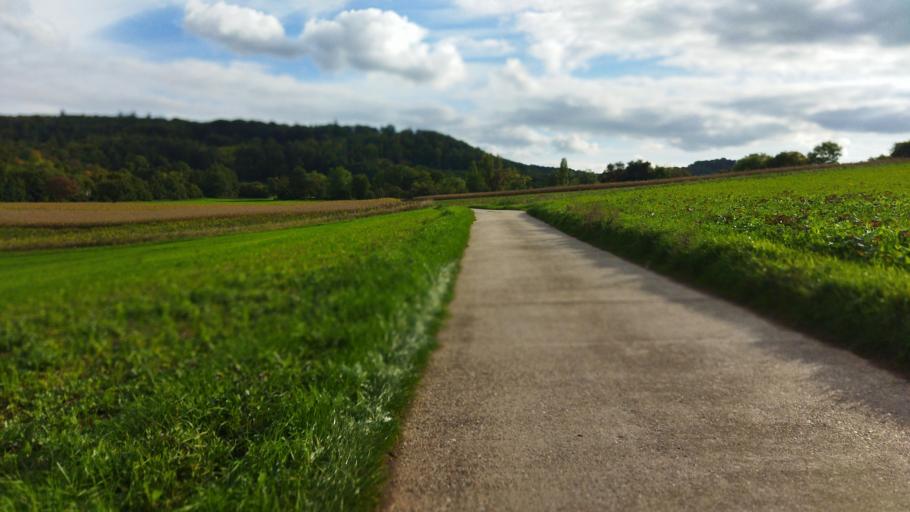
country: DE
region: Baden-Wuerttemberg
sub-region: Karlsruhe Region
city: Kurnbach
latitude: 49.0737
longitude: 8.8560
